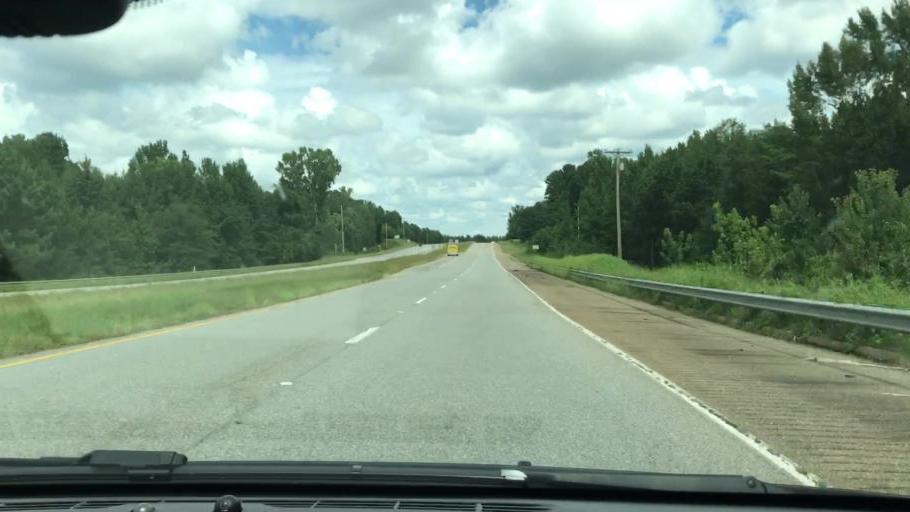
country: US
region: Georgia
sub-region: Stewart County
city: Lumpkin
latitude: 32.1274
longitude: -84.8236
